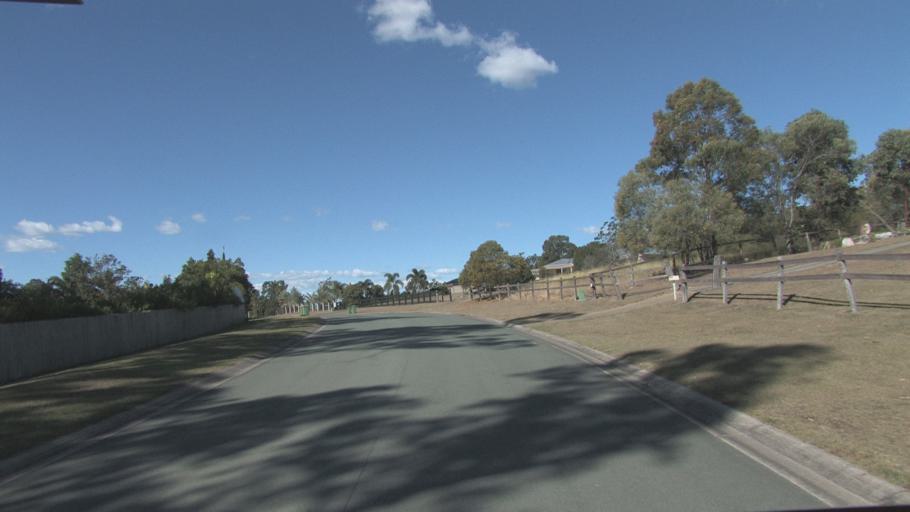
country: AU
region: Queensland
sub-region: Ipswich
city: Springfield Lakes
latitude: -27.7343
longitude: 152.9070
